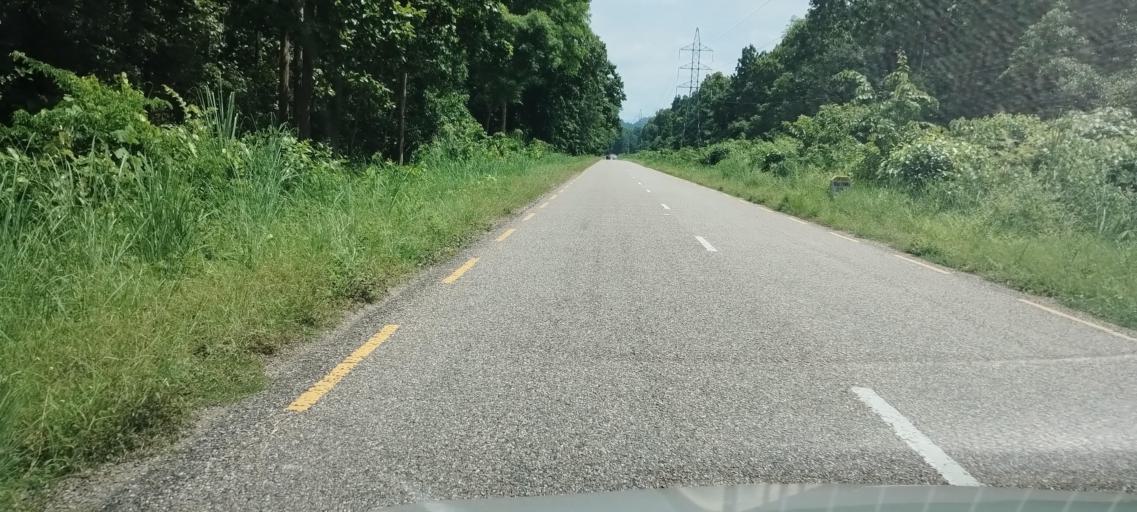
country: NP
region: Mid Western
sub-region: Bheri Zone
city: Bardiya
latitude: 28.4306
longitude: 81.3562
